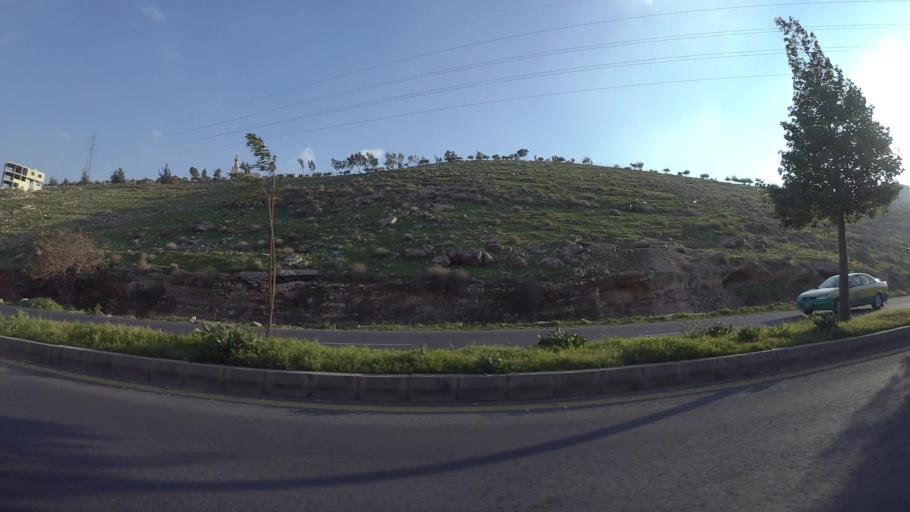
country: JO
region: Amman
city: Amman
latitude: 31.9813
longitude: 35.9644
